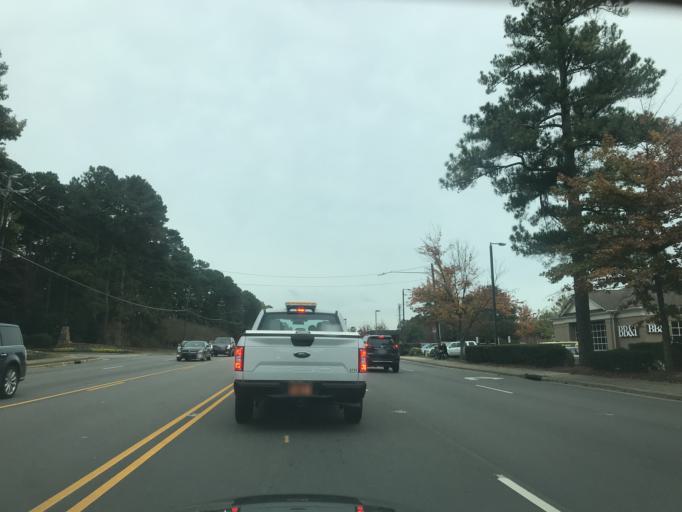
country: US
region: North Carolina
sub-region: Wake County
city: West Raleigh
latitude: 35.8748
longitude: -78.6231
